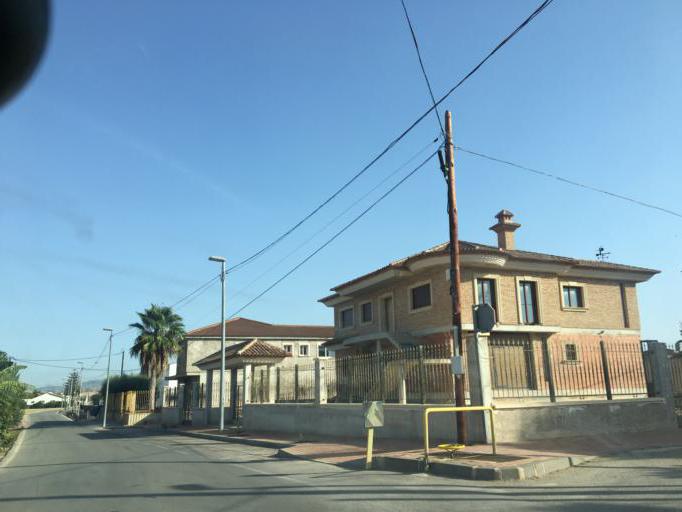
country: ES
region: Murcia
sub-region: Murcia
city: Santomera
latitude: 38.0314
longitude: -1.0689
